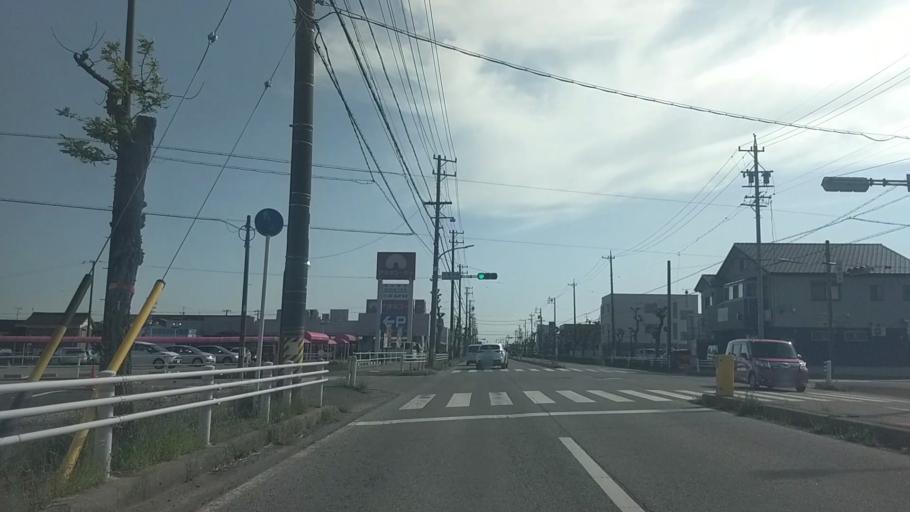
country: JP
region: Aichi
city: Anjo
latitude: 34.9528
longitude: 137.0980
